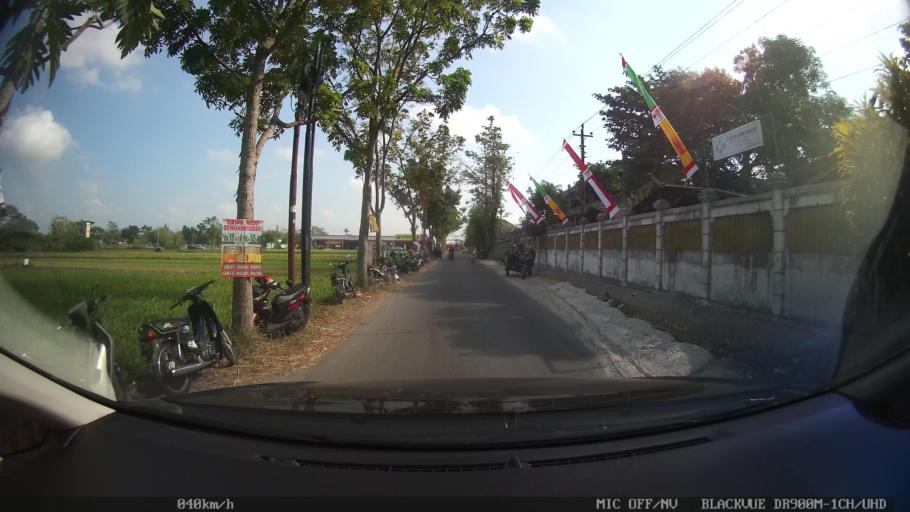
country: ID
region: Daerah Istimewa Yogyakarta
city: Gamping Lor
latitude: -7.8063
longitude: 110.2995
